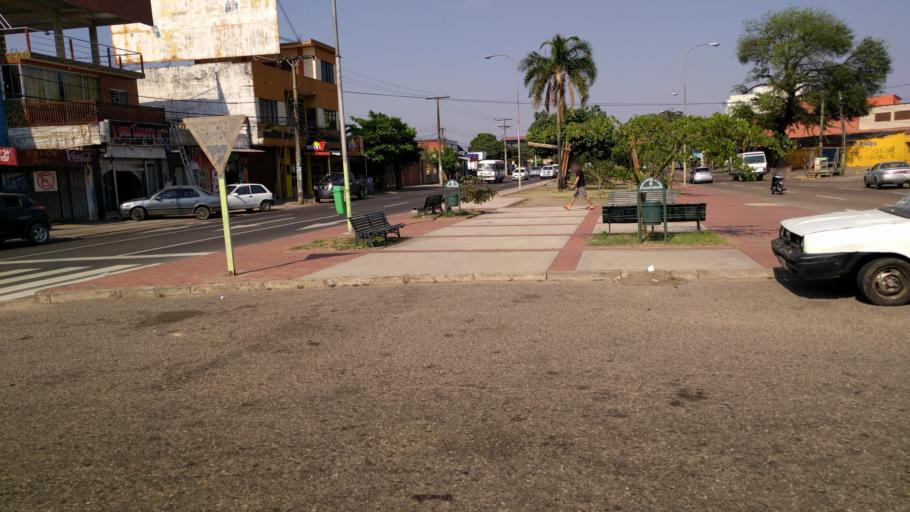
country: BO
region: Santa Cruz
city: Santa Cruz de la Sierra
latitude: -17.7958
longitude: -63.1570
